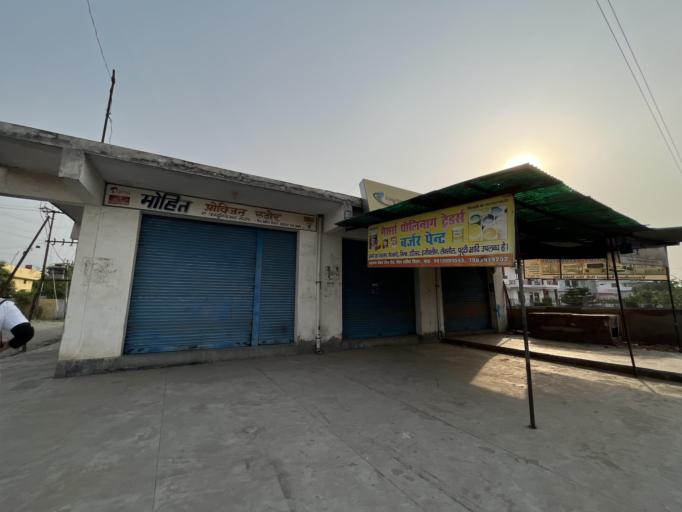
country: IN
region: Uttarakhand
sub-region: Naini Tal
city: Haldwani
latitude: 29.1990
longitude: 79.4825
